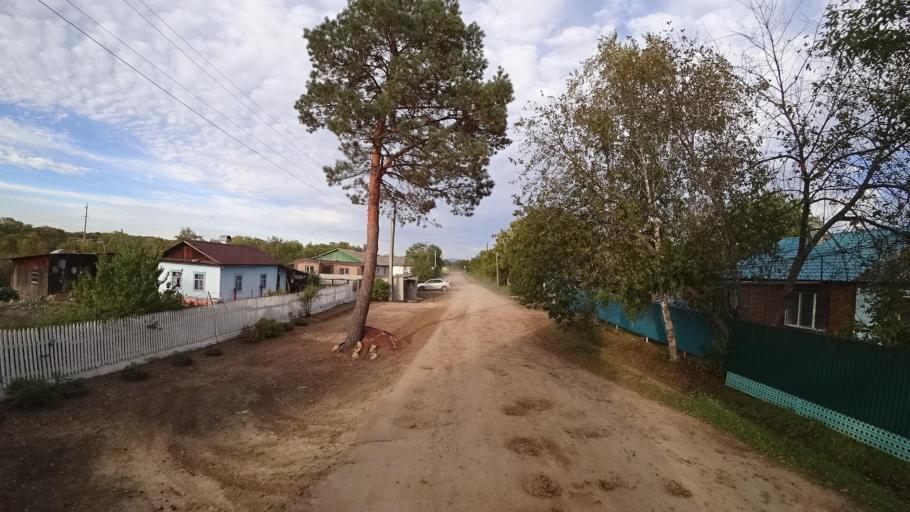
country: RU
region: Primorskiy
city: Yakovlevka
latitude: 44.4196
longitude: 133.4488
